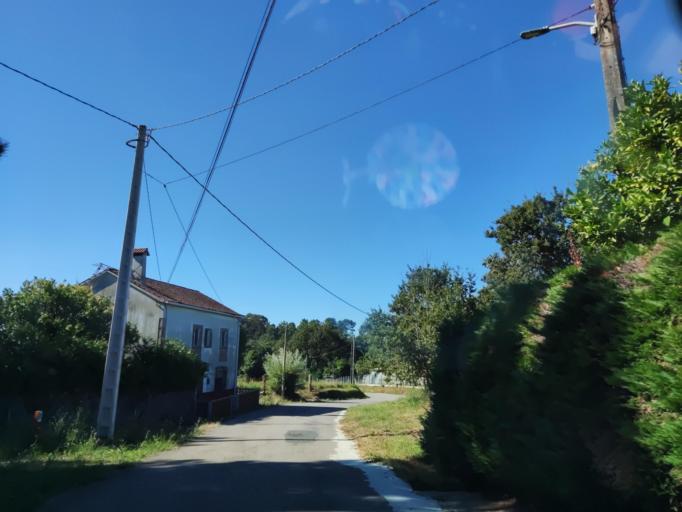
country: ES
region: Galicia
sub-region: Provincia da Coruna
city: Rianxo
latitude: 42.6912
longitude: -8.8467
